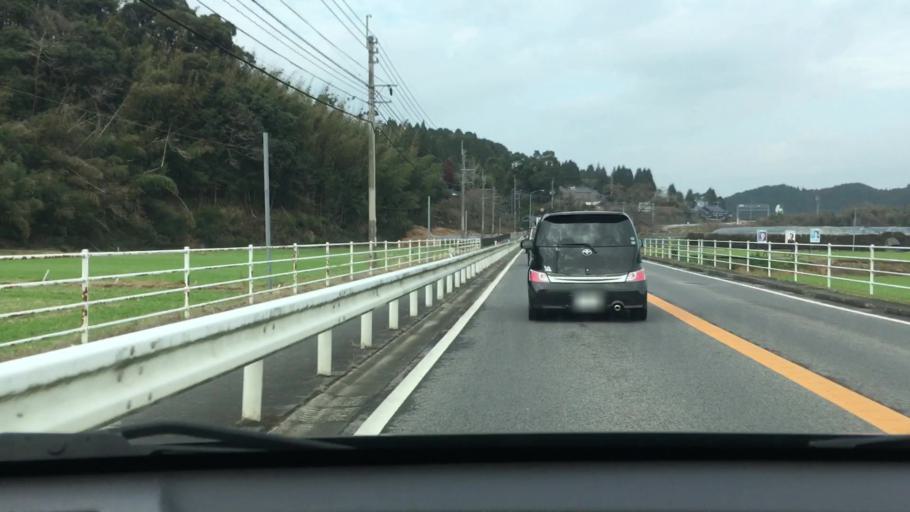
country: JP
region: Saga Prefecture
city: Imaricho-ko
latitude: 33.3282
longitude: 129.9300
